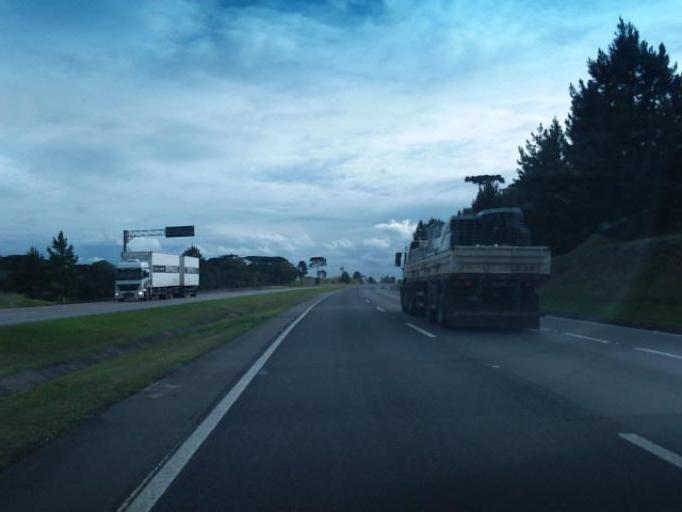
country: BR
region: Parana
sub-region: Quatro Barras
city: Quatro Barras
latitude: -25.3649
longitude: -49.0421
